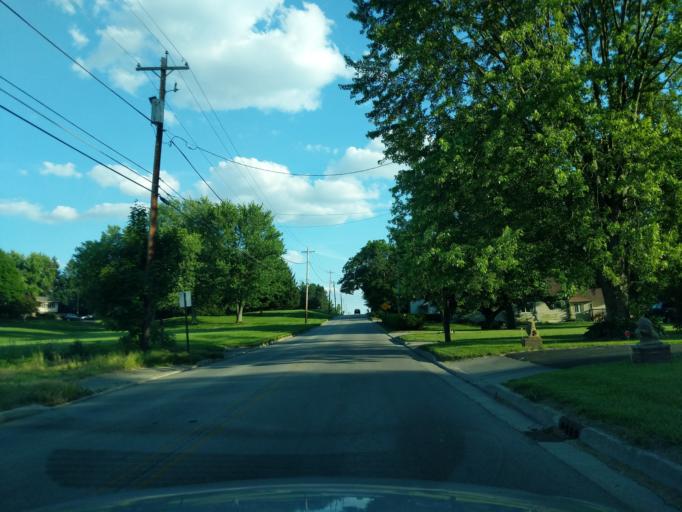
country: US
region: Indiana
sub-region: Huntington County
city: Huntington
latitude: 40.8701
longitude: -85.4709
